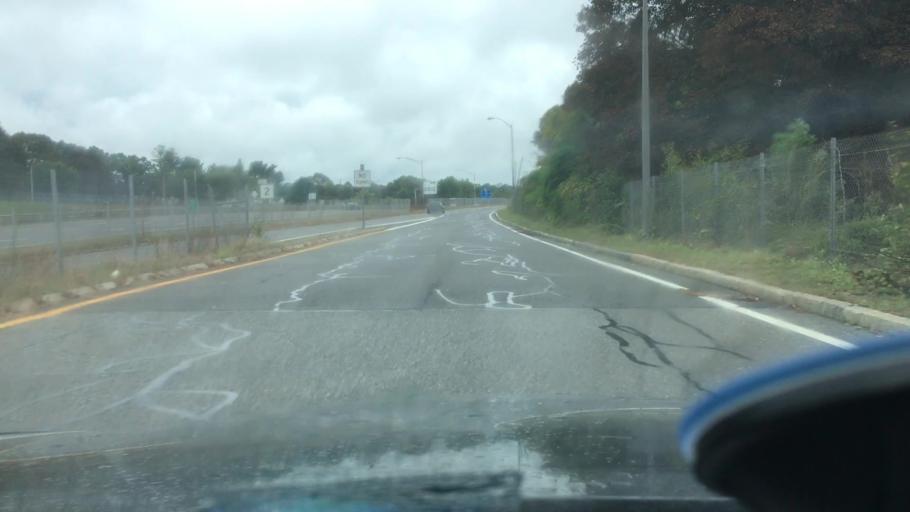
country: US
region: Massachusetts
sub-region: Middlesex County
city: Belmont
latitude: 42.4167
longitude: -71.2020
